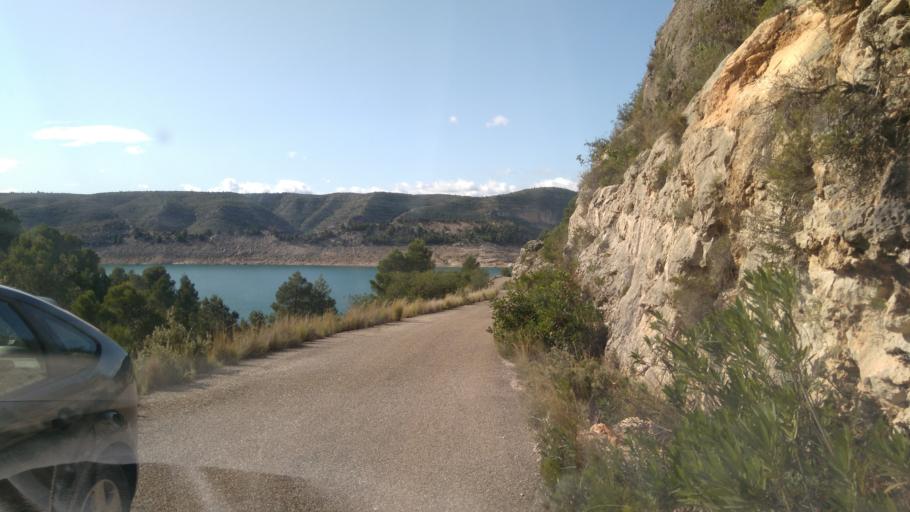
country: ES
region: Valencia
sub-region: Provincia de Valencia
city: Sumacarcer
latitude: 39.1528
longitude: -0.6527
